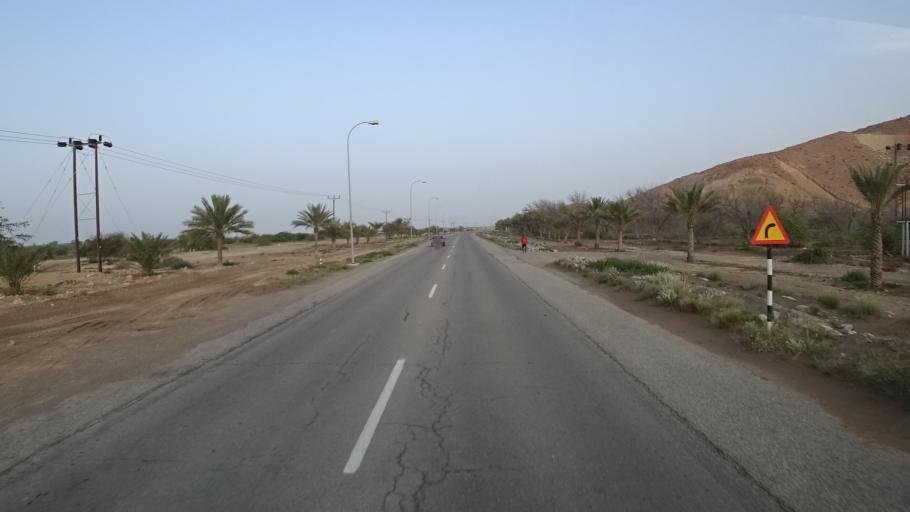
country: OM
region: Muhafazat Masqat
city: Muscat
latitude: 23.2158
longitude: 58.9305
